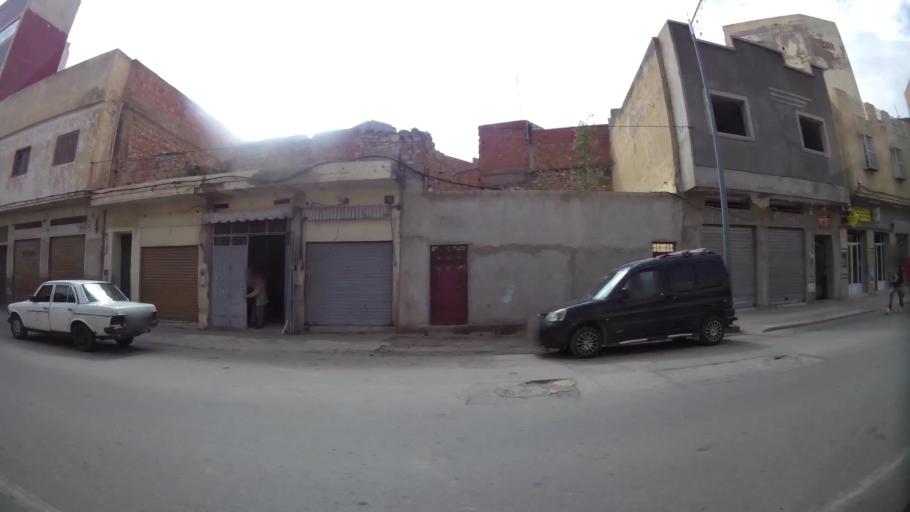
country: MA
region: Oriental
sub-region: Oujda-Angad
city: Oujda
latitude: 34.6855
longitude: -1.9090
